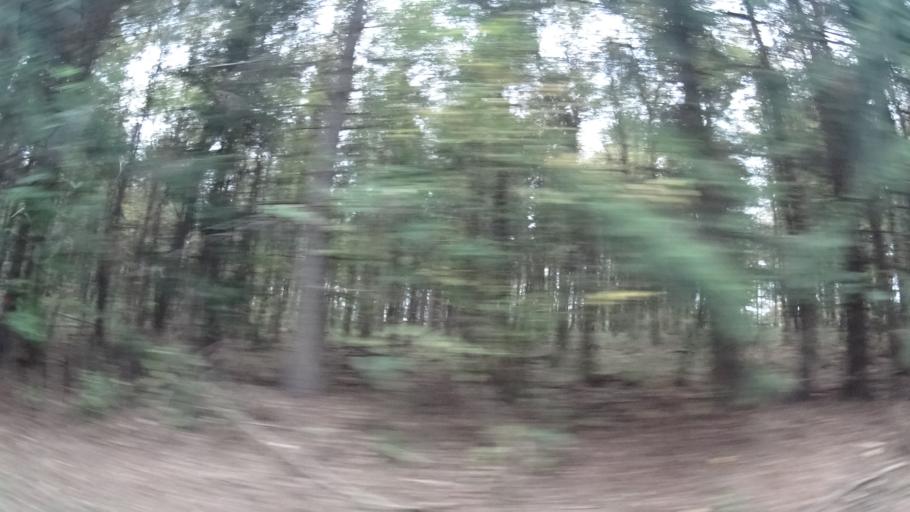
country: DE
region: Thuringia
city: Birx
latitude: 50.5548
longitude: 10.0434
